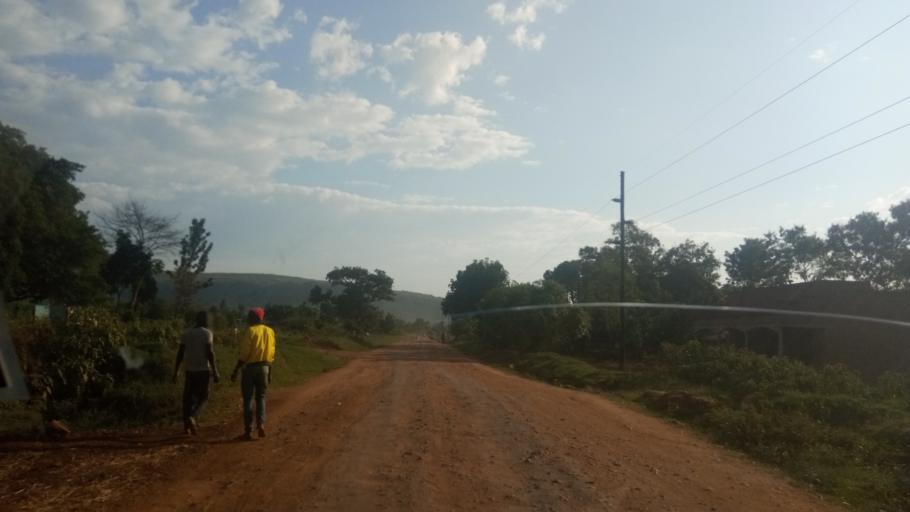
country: UG
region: Eastern Region
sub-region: Kapchorwa District
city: Kapchorwa
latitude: 1.4128
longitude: 34.3489
